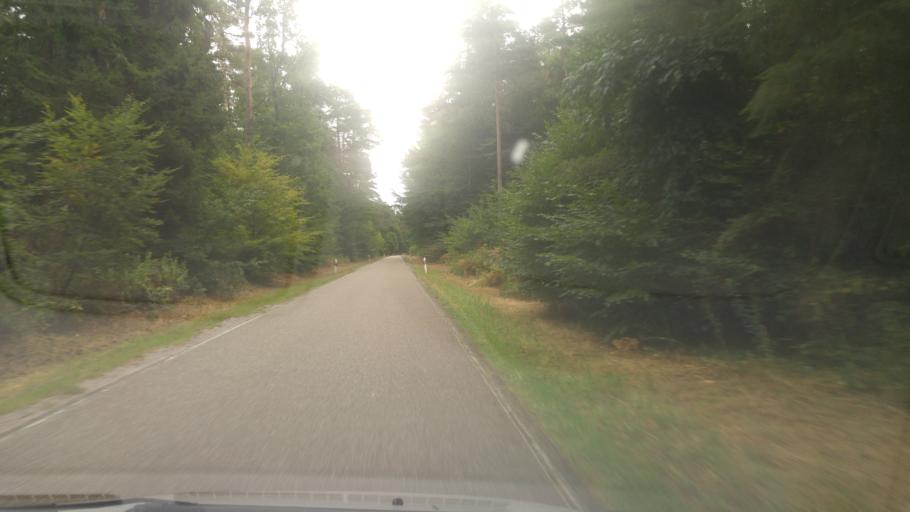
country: DE
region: Rheinland-Pfalz
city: Steinfeld
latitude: 49.0146
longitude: 8.0519
